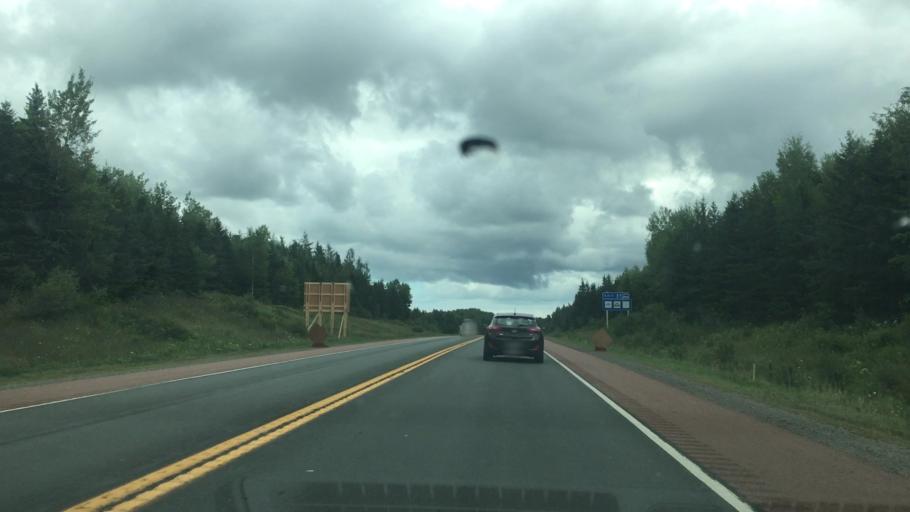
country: CA
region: Nova Scotia
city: Antigonish
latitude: 45.5918
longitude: -62.0668
